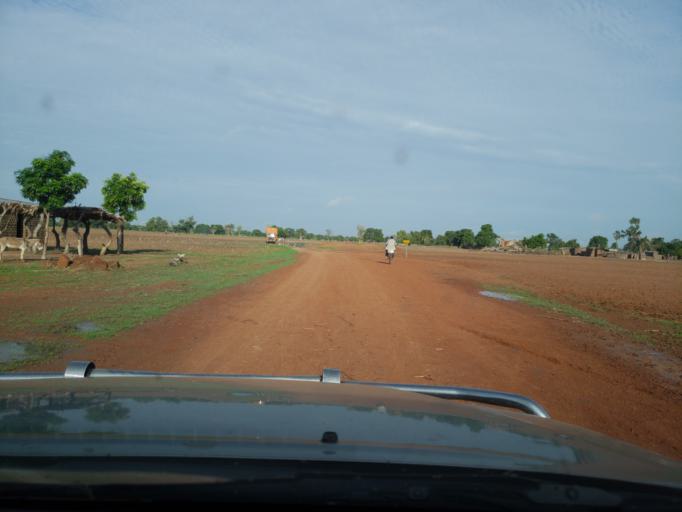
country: ML
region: Sikasso
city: Koutiala
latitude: 12.4217
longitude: -5.6877
